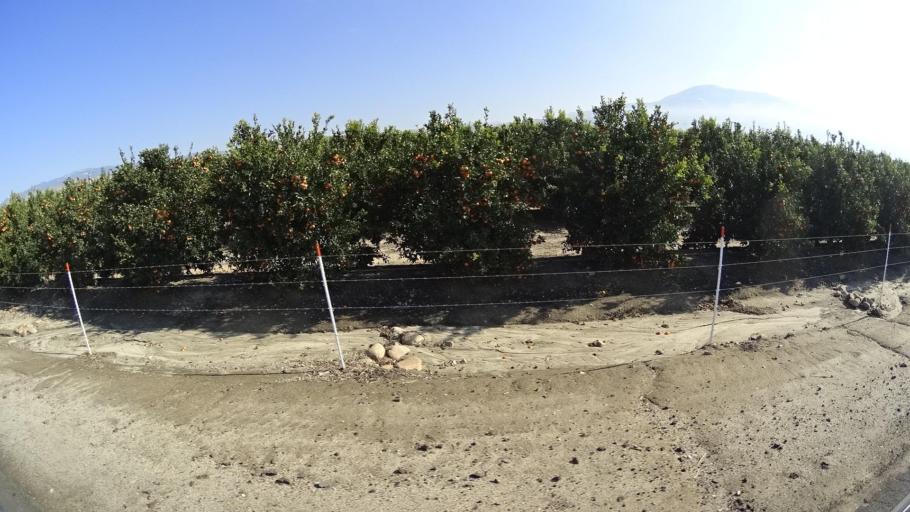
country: US
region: California
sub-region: Kern County
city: Arvin
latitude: 35.2764
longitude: -118.7707
